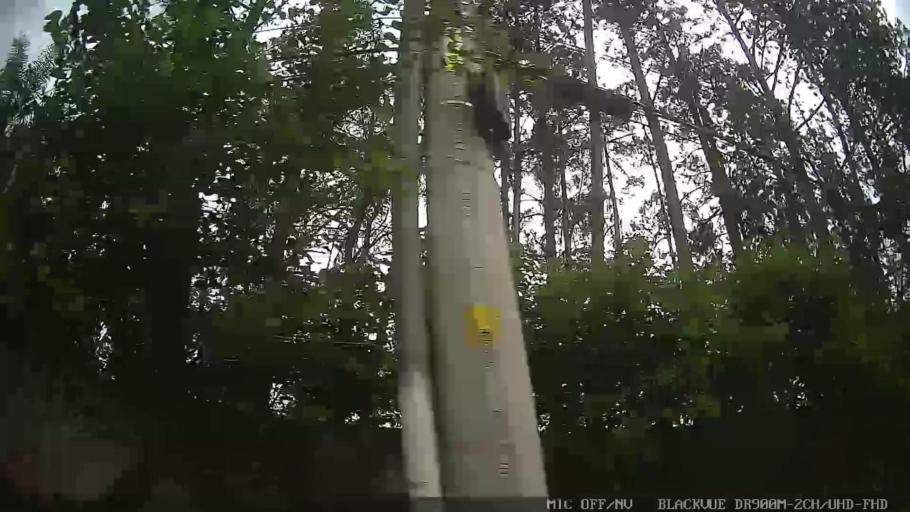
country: BR
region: Sao Paulo
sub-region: Serra Negra
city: Serra Negra
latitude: -22.6089
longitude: -46.6976
